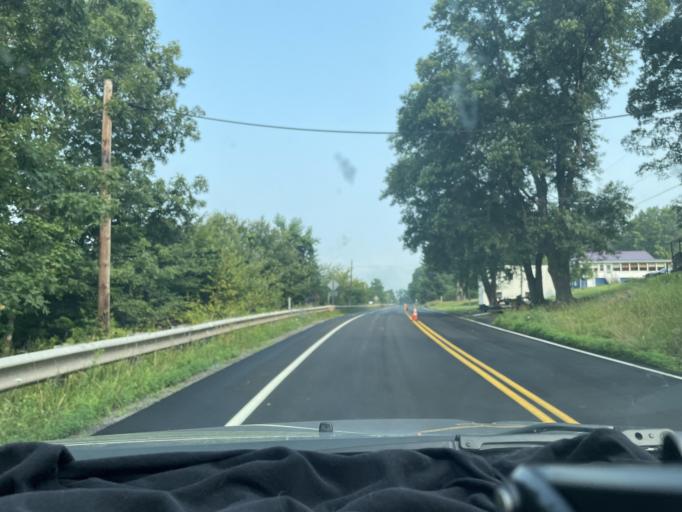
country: US
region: Maryland
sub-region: Garrett County
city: Mountain Lake Park
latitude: 39.2892
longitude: -79.3505
